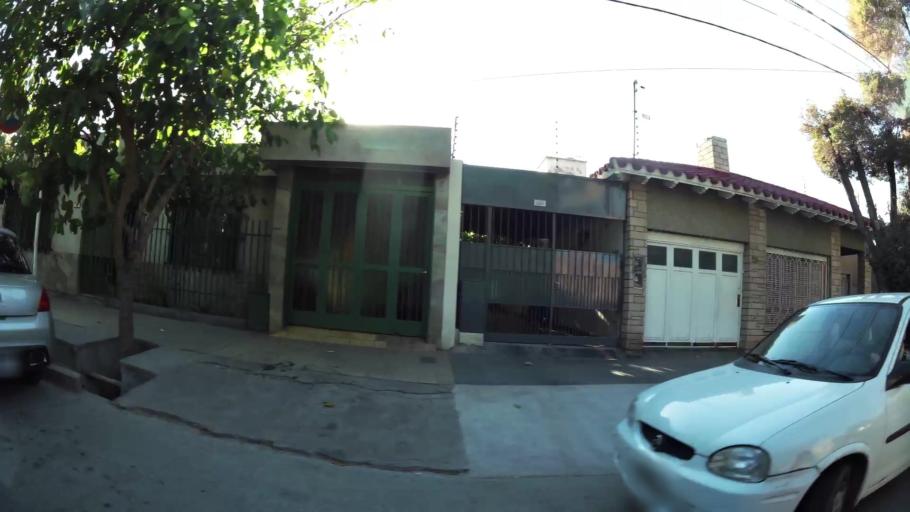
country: AR
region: Mendoza
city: Las Heras
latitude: -32.8681
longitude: -68.8273
